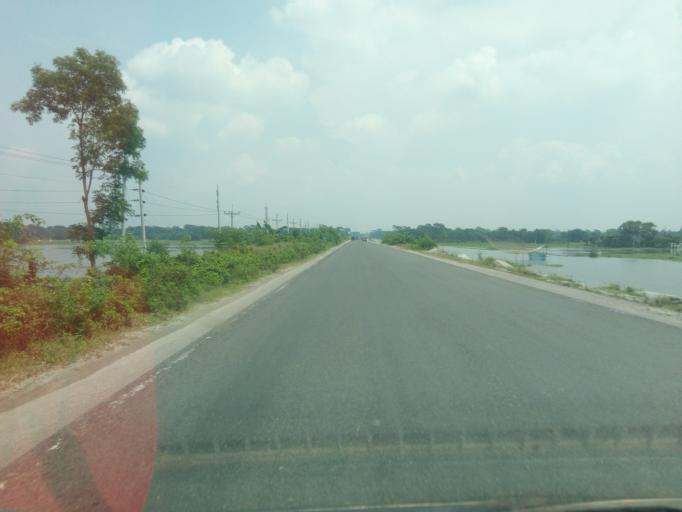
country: BD
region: Dhaka
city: Char Bhadrasan
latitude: 23.3782
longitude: 90.0132
